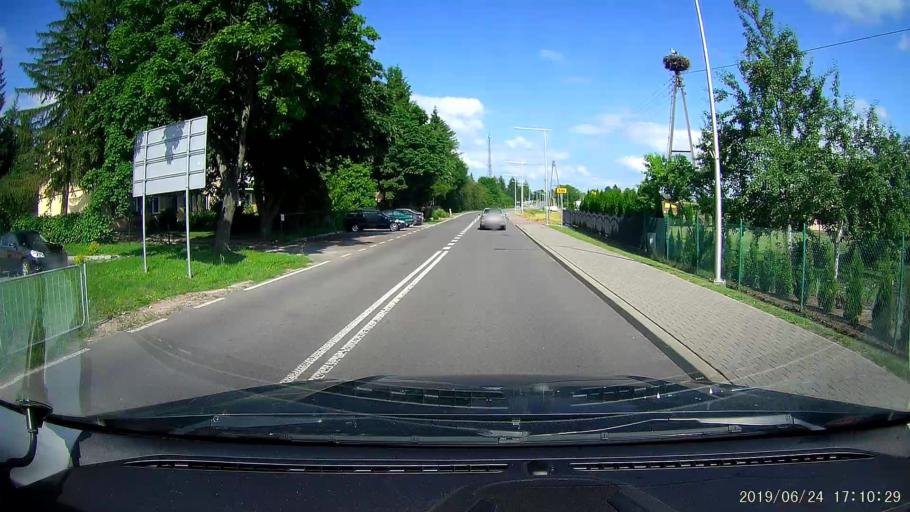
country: PL
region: Lublin Voivodeship
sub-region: Powiat hrubieszowski
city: Dolhobyczow
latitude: 50.5863
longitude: 24.0360
